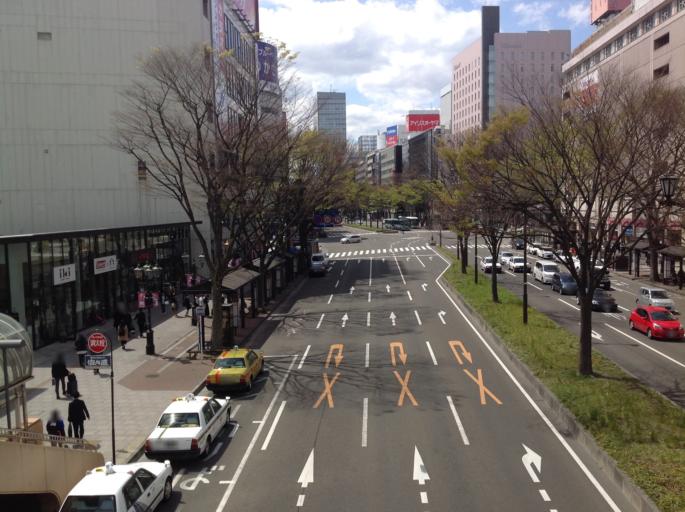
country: JP
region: Miyagi
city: Sendai-shi
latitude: 38.2608
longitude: 140.8808
